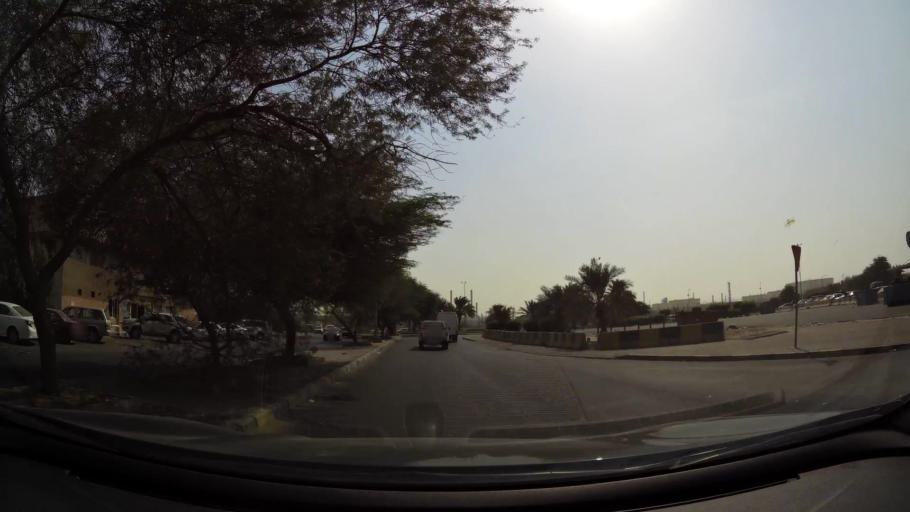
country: KW
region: Al Ahmadi
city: Al Fahahil
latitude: 29.0711
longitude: 48.1259
